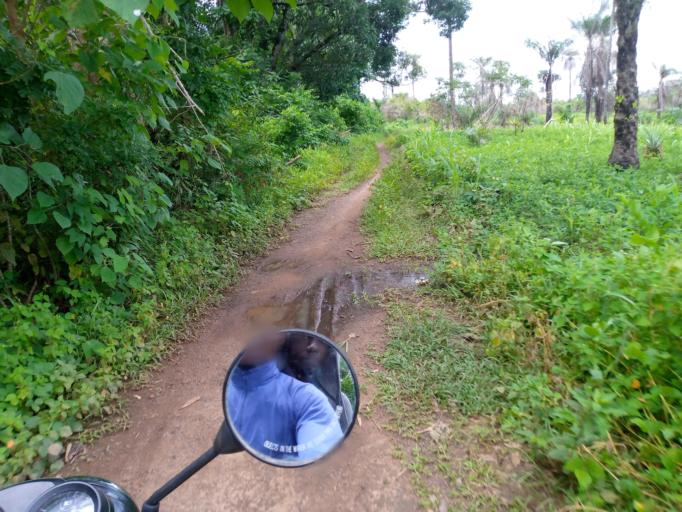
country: SL
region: Northern Province
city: Mange
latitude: 8.9915
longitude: -12.7728
